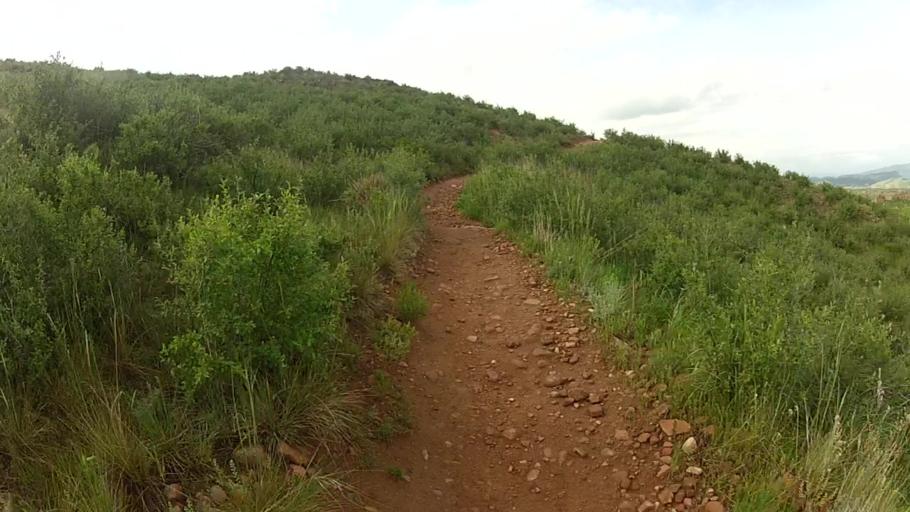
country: US
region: Colorado
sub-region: Larimer County
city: Loveland
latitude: 40.4326
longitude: -105.1624
